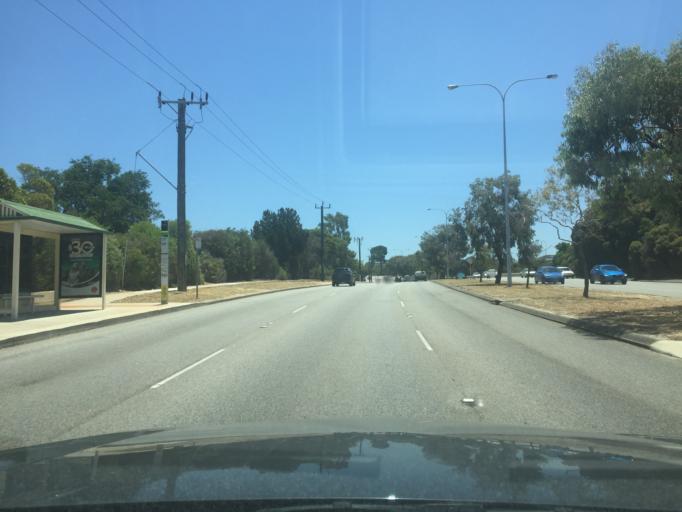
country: AU
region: Western Australia
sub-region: Melville
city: Kardinya
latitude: -32.0683
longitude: 115.8112
